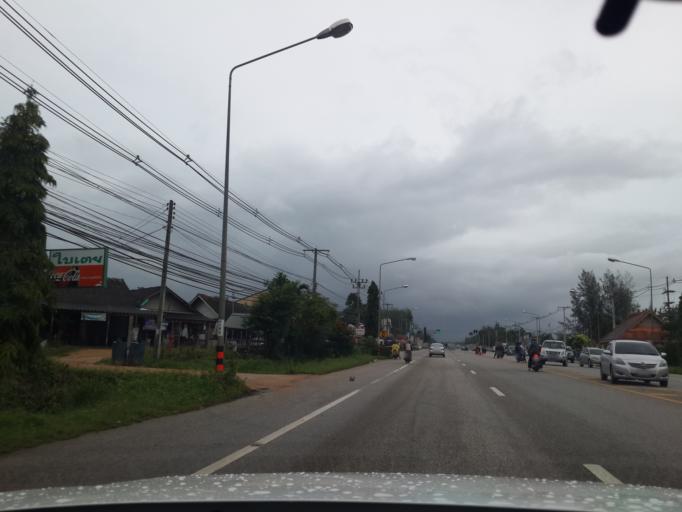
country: TH
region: Songkhla
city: Khlong Hoi Khong
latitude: 6.9566
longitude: 100.4213
